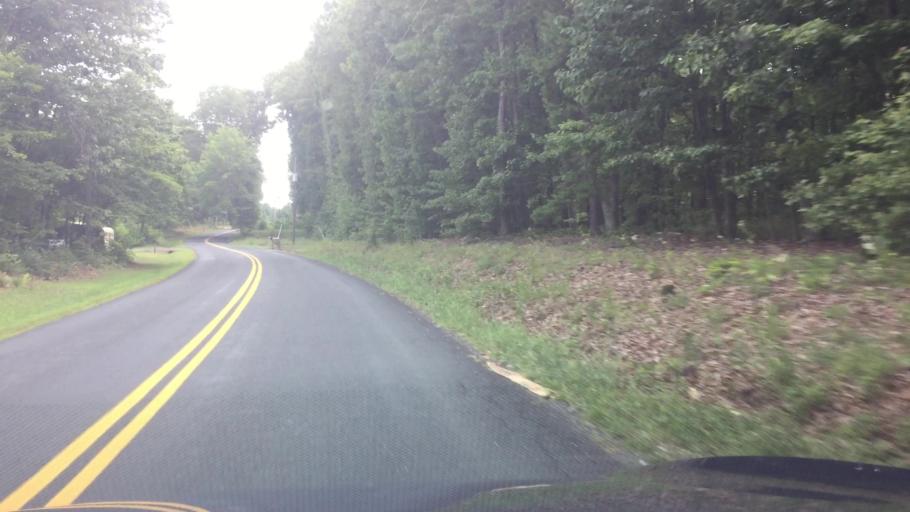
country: US
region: Virginia
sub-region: Appomattox County
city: Appomattox
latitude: 37.2884
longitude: -78.8519
